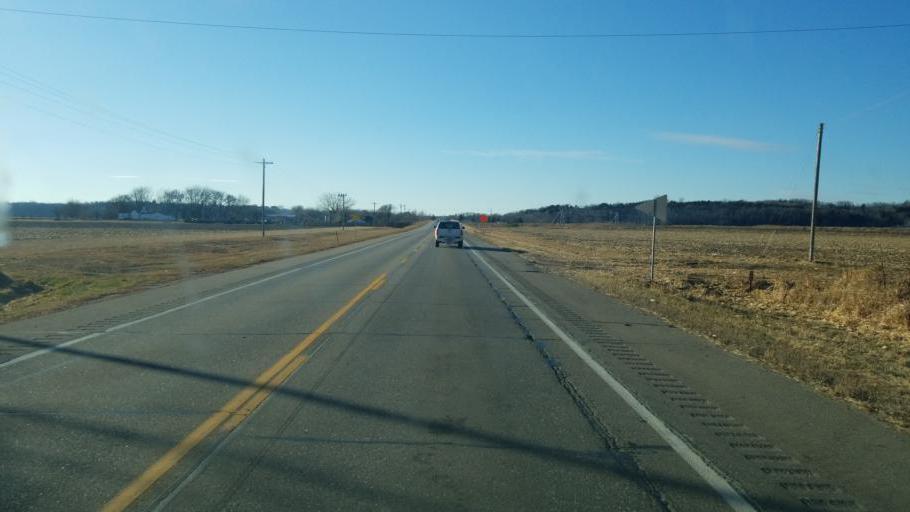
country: US
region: South Dakota
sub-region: Union County
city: Dakota Dunes
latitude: 42.4484
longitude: -96.5507
